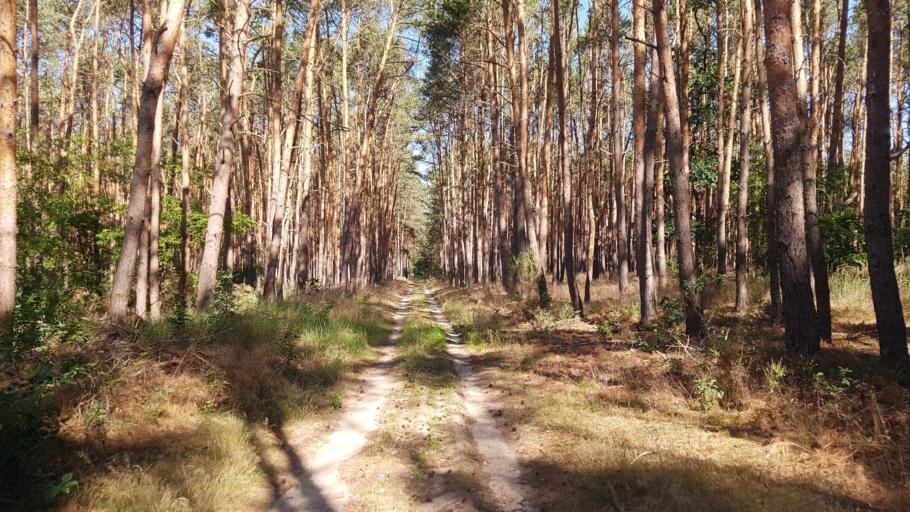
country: DE
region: Brandenburg
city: Juterbog
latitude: 51.9751
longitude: 13.1460
